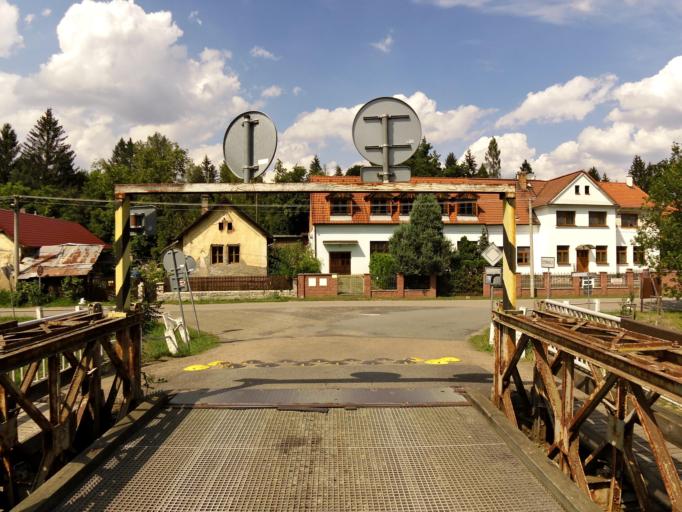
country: CZ
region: Central Bohemia
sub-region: Okres Benesov
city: Cercany
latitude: 49.8666
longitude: 14.7171
